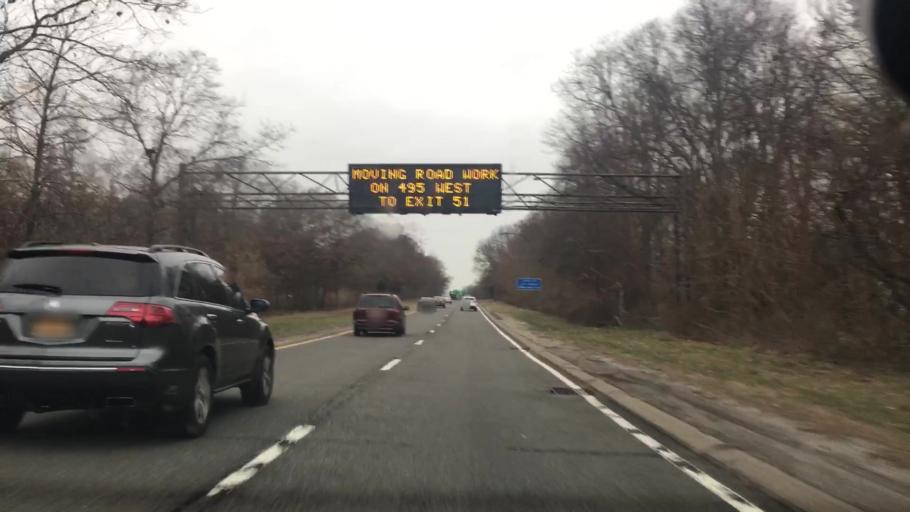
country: US
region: New York
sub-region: Suffolk County
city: Commack
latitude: 40.8178
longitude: -73.2771
